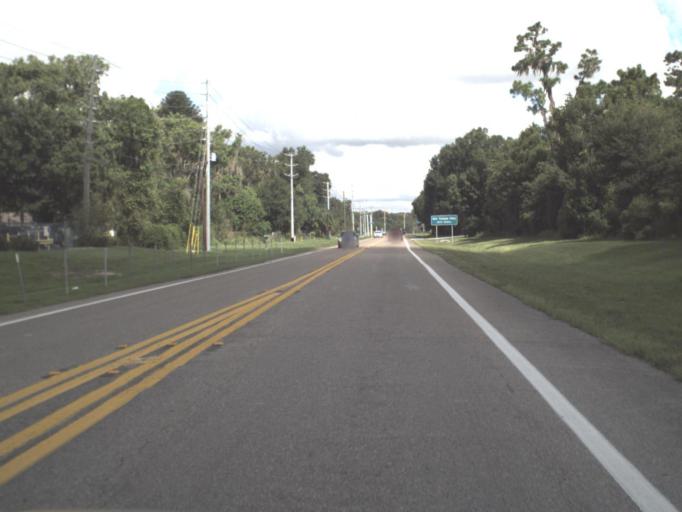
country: US
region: Florida
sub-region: Polk County
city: Winston
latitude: 28.0253
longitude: -82.0165
